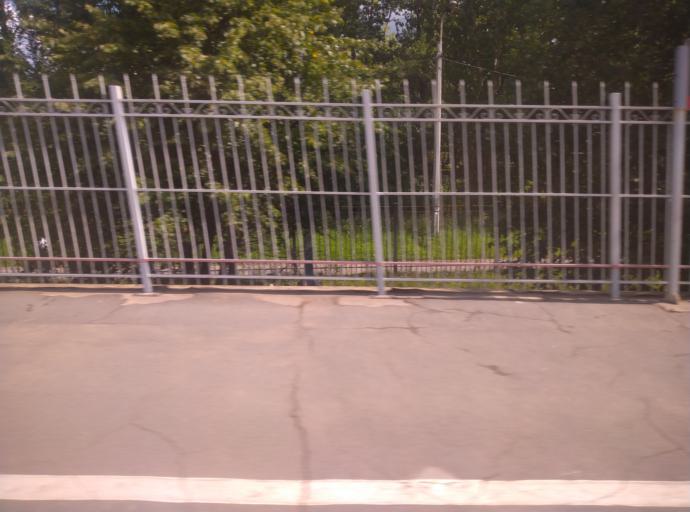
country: RU
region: St.-Petersburg
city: Kolpino
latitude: 59.7503
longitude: 30.6137
